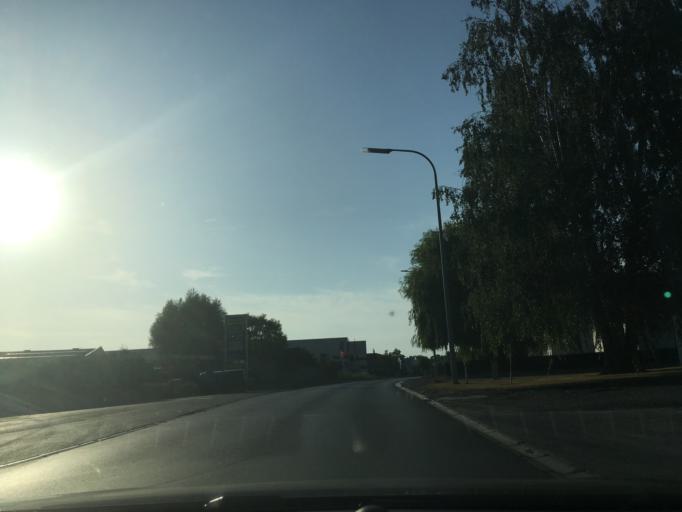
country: BE
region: Flanders
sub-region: Provincie West-Vlaanderen
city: Tielt
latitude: 50.9988
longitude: 3.3478
